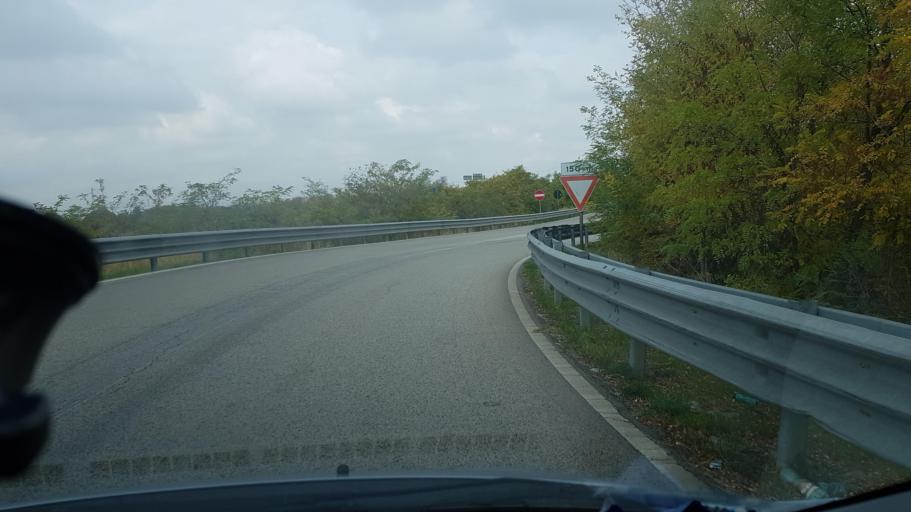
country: IT
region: Apulia
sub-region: Provincia di Foggia
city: Foggia
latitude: 41.4940
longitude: 15.5601
